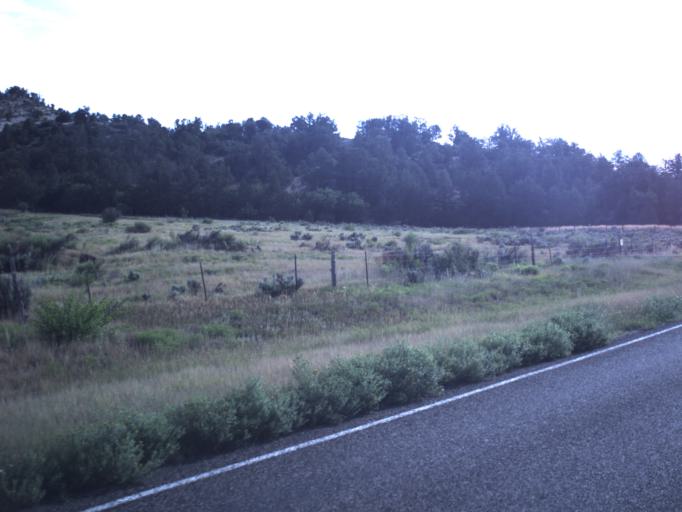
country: US
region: Utah
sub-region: Washington County
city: Hildale
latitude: 37.2384
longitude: -112.8375
